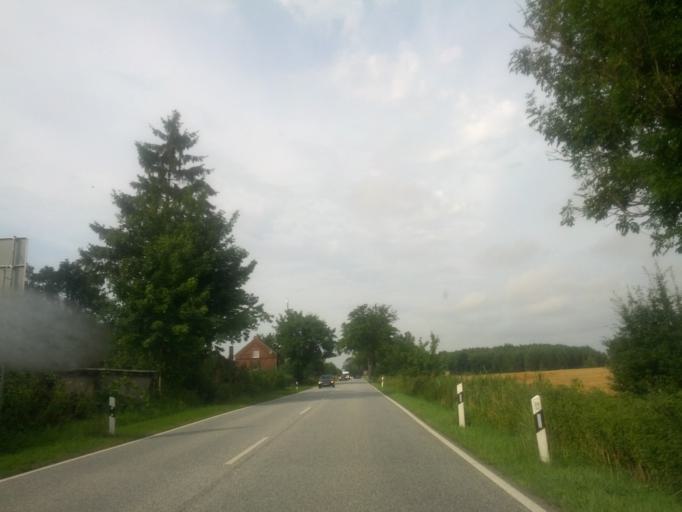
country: DE
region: Mecklenburg-Vorpommern
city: Sellin
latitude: 53.9568
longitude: 11.6150
